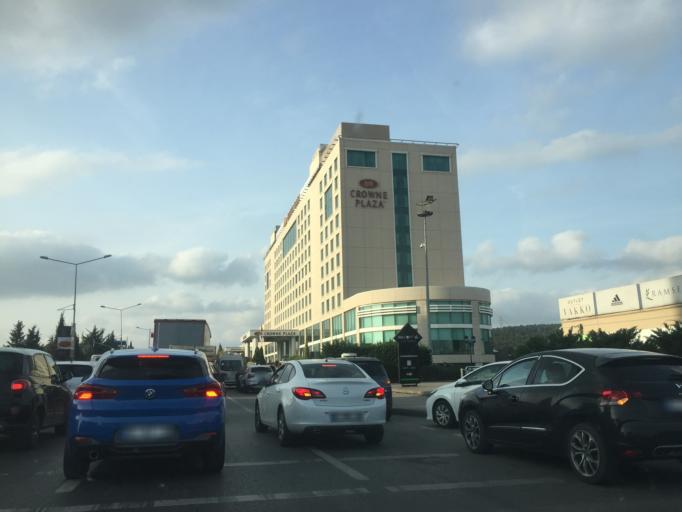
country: TR
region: Istanbul
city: Sultanbeyli
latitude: 40.9373
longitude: 29.3238
